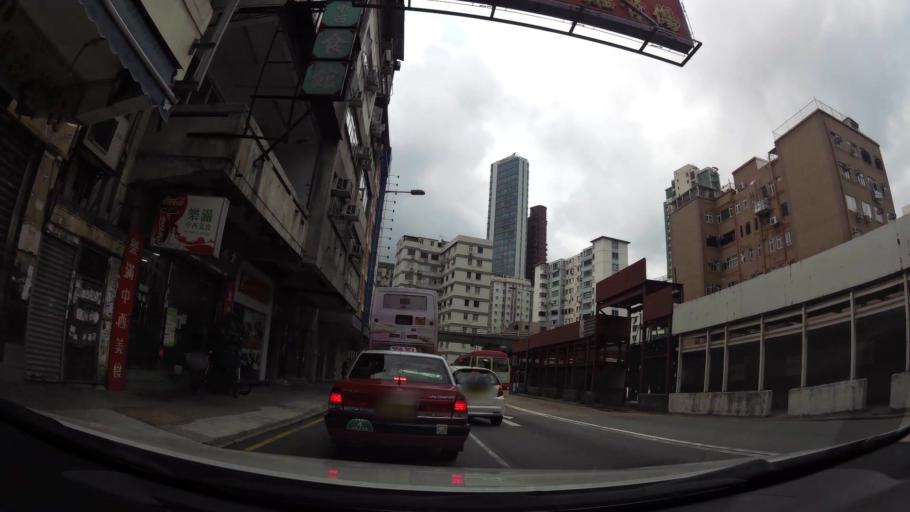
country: HK
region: Kowloon City
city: Kowloon
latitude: 22.3279
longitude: 114.1870
